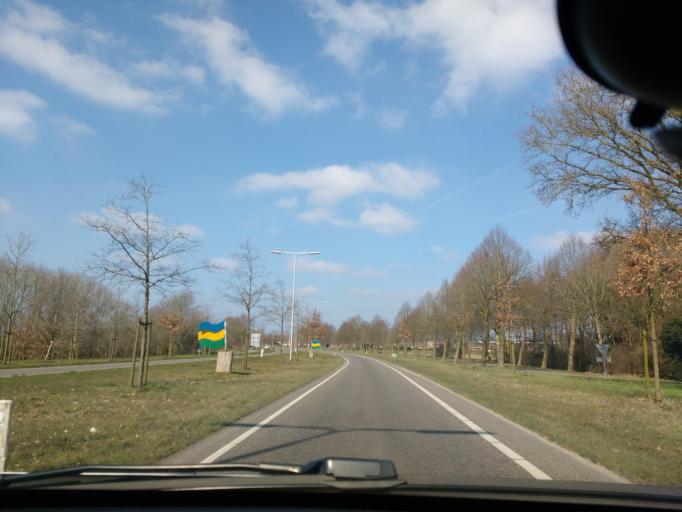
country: NL
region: Limburg
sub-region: Gemeente Gennep
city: Gennep
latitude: 51.7121
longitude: 5.9645
